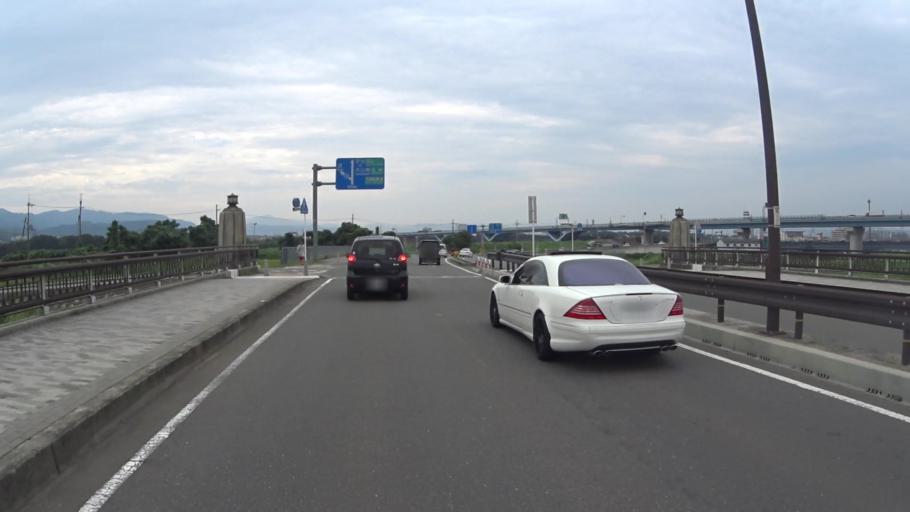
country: JP
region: Kyoto
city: Yawata
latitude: 34.8927
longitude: 135.7007
